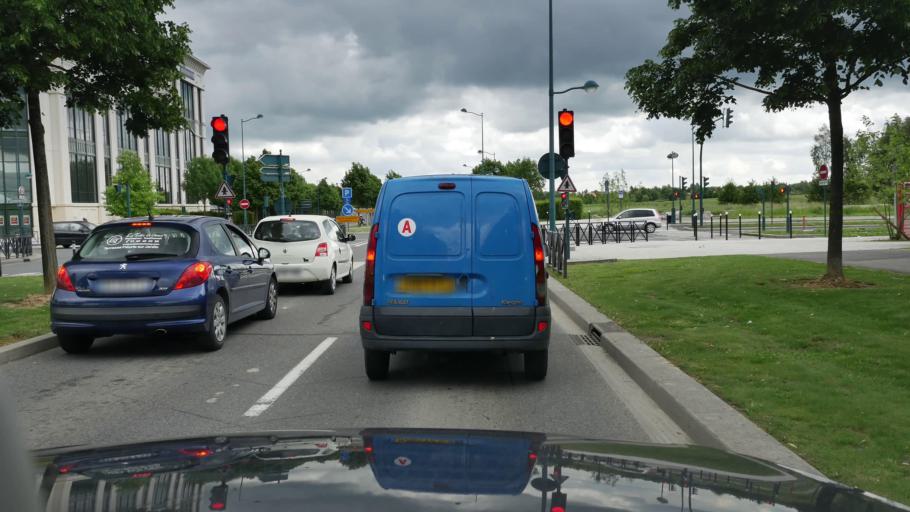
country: FR
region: Ile-de-France
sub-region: Departement de Seine-et-Marne
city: Serris
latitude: 48.8536
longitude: 2.7739
